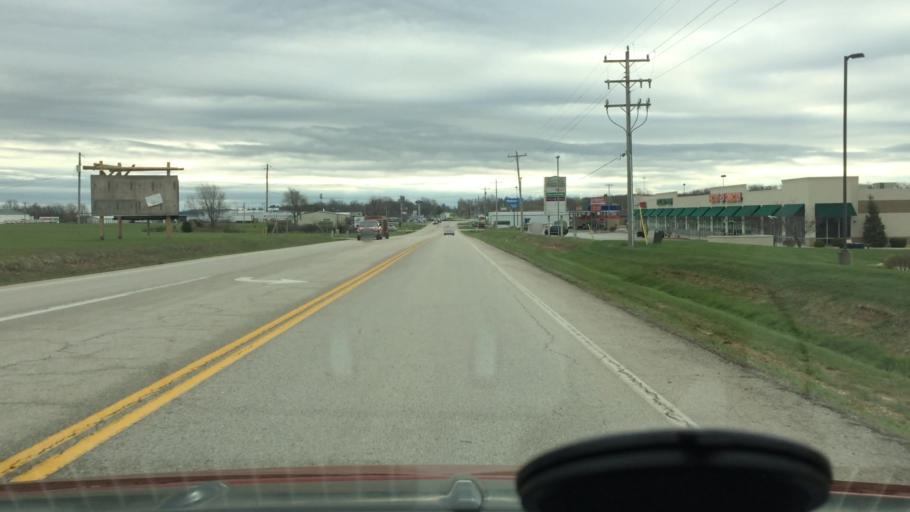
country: US
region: Missouri
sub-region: Webster County
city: Marshfield
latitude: 37.3401
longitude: -92.9417
